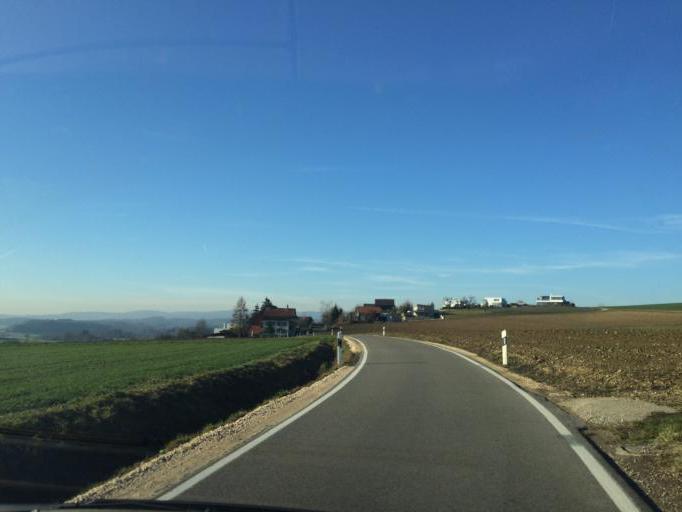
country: CH
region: Thurgau
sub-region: Frauenfeld District
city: Diessenhofen
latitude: 47.7018
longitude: 8.7311
